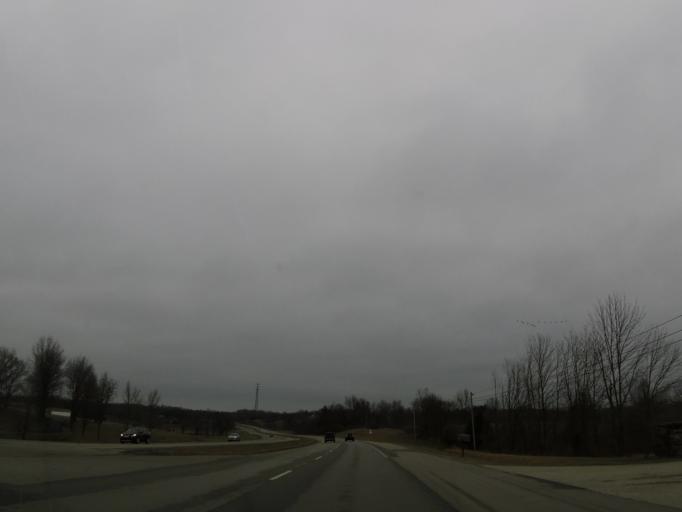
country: US
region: Kentucky
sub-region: Anderson County
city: Lawrenceburg
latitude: 38.1040
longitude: -84.9172
